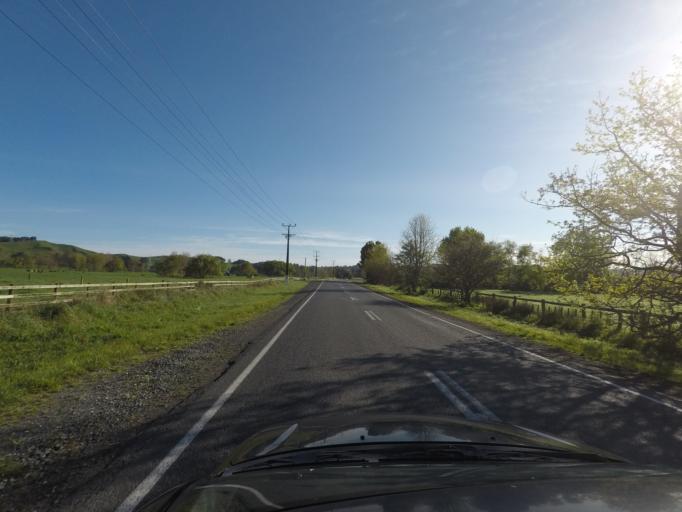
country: NZ
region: Auckland
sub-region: Auckland
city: Red Hill
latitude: -37.0073
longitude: 174.9538
